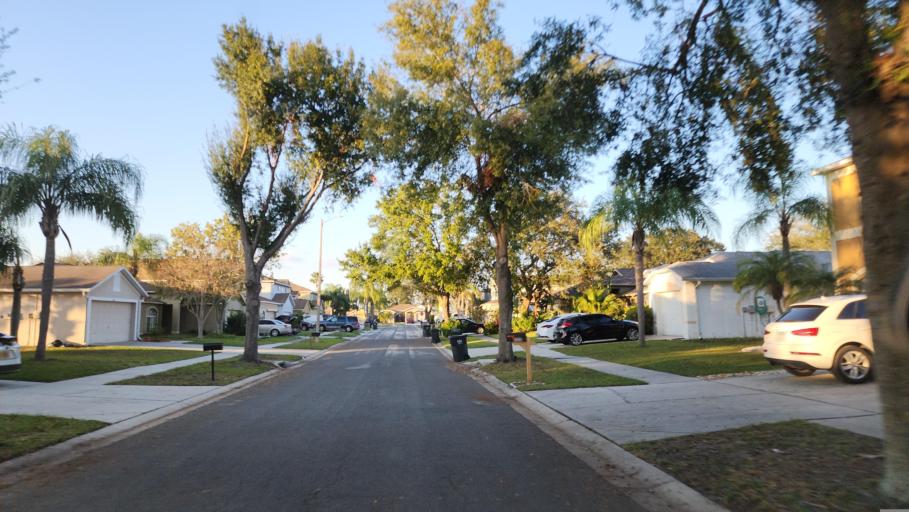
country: US
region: Florida
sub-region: Hillsborough County
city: Balm
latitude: 27.8050
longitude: -82.3051
